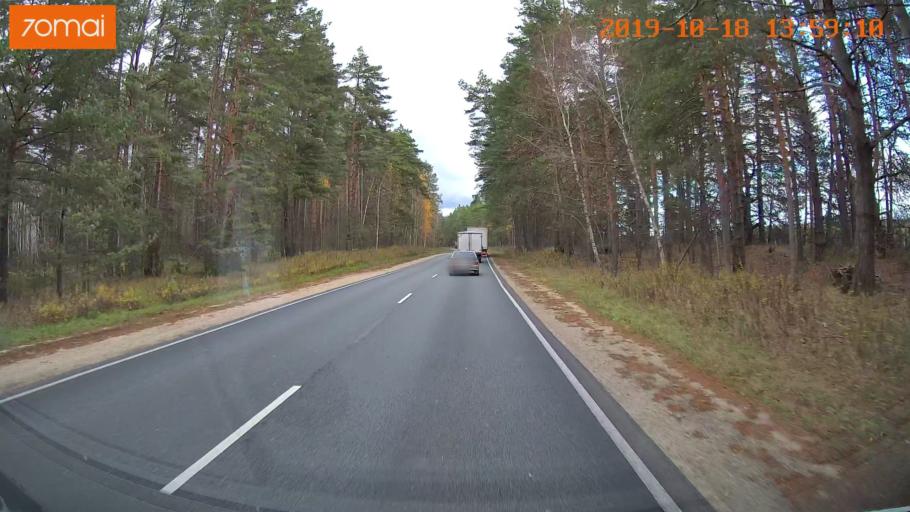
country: RU
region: Rjazan
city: Spas-Klepiki
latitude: 55.0918
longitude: 40.0609
